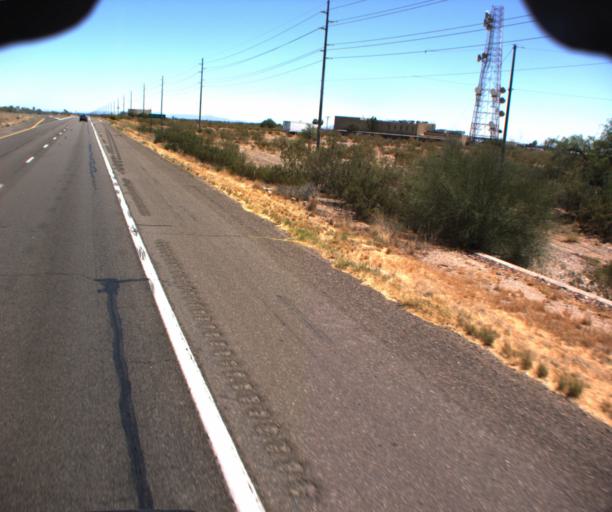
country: US
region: Arizona
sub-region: Maricopa County
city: Sun City West
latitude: 33.7390
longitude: -112.4791
